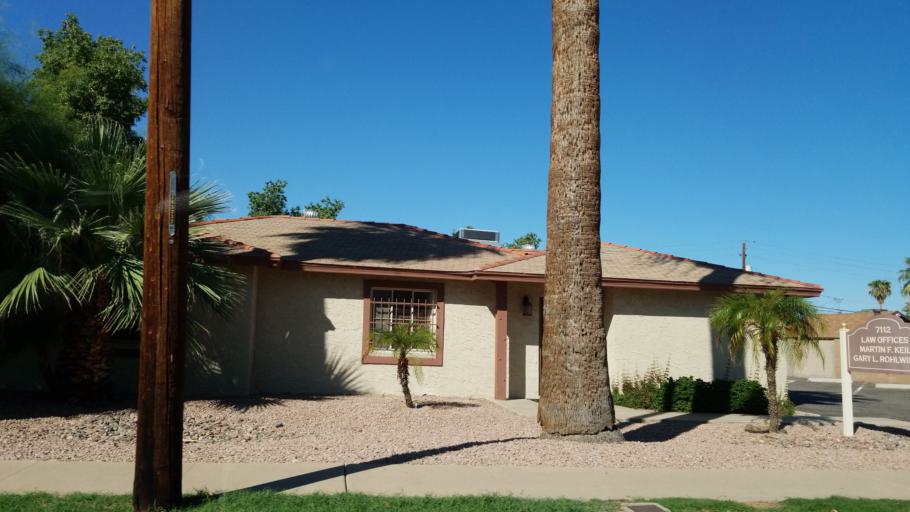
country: US
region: Arizona
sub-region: Maricopa County
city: Glendale
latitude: 33.5403
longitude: -112.1774
